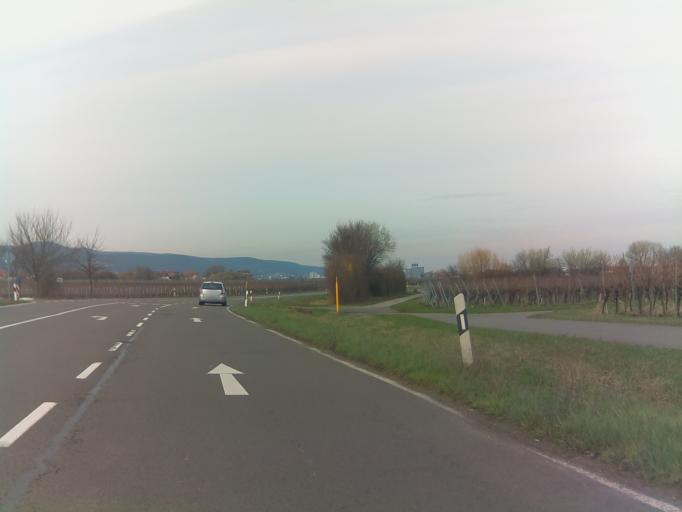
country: DE
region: Rheinland-Pfalz
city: Maikammer
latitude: 49.3120
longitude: 8.1444
